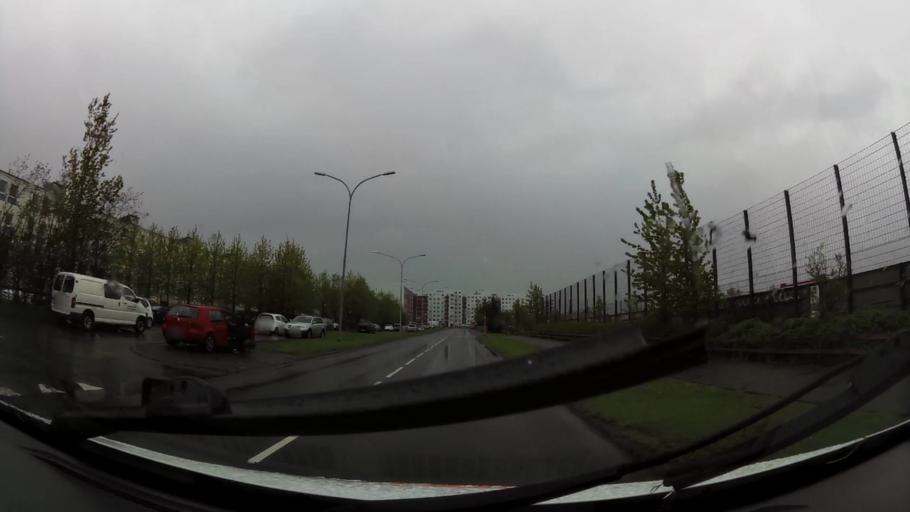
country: IS
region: Capital Region
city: Reykjavik
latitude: 64.1016
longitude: -21.8198
